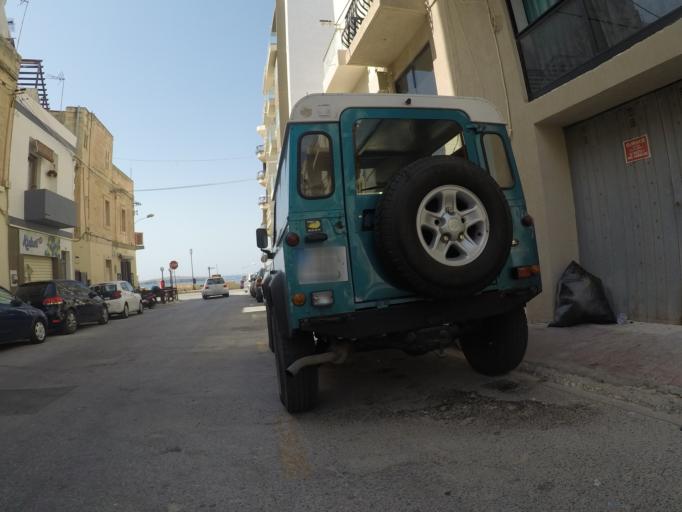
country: MT
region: Saint Paul's Bay
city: San Pawl il-Bahar
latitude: 35.9495
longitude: 14.4092
